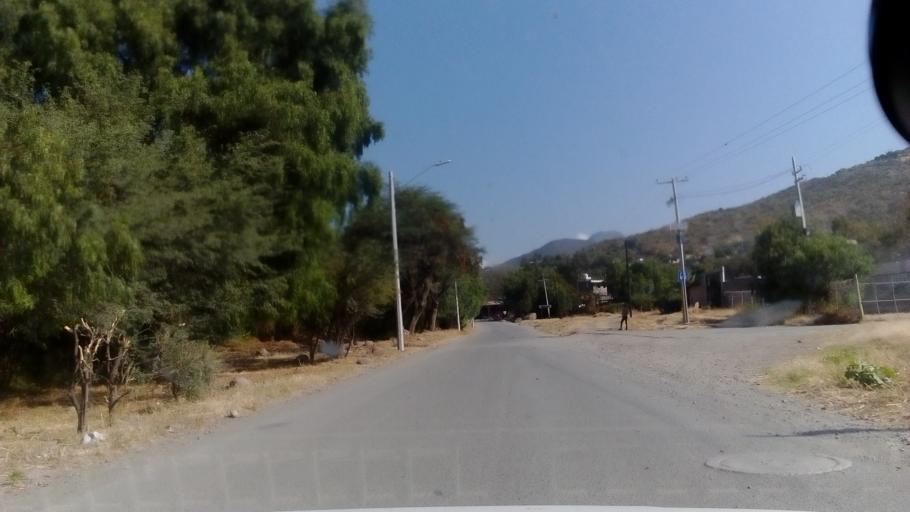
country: MX
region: Guanajuato
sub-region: Leon
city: Medina
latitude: 21.1449
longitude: -101.6094
